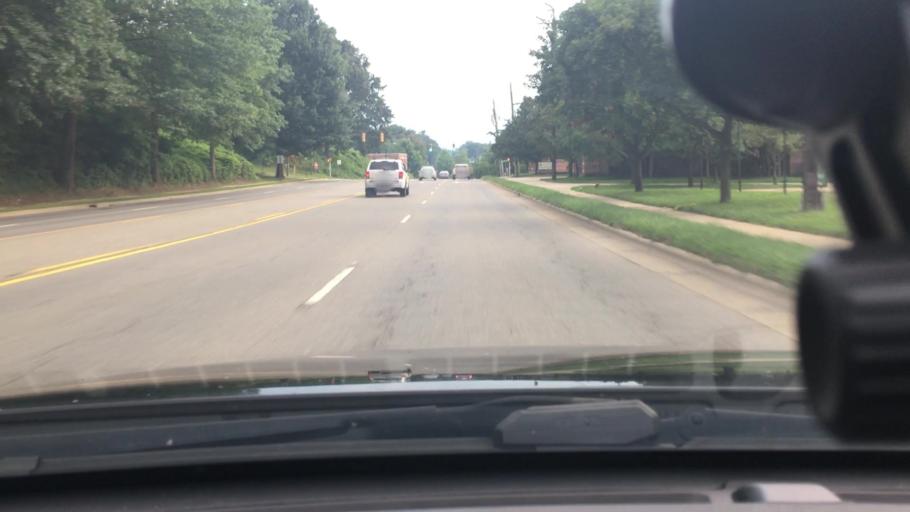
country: US
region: North Carolina
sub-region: Buncombe County
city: Asheville
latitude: 35.5935
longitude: -82.5482
